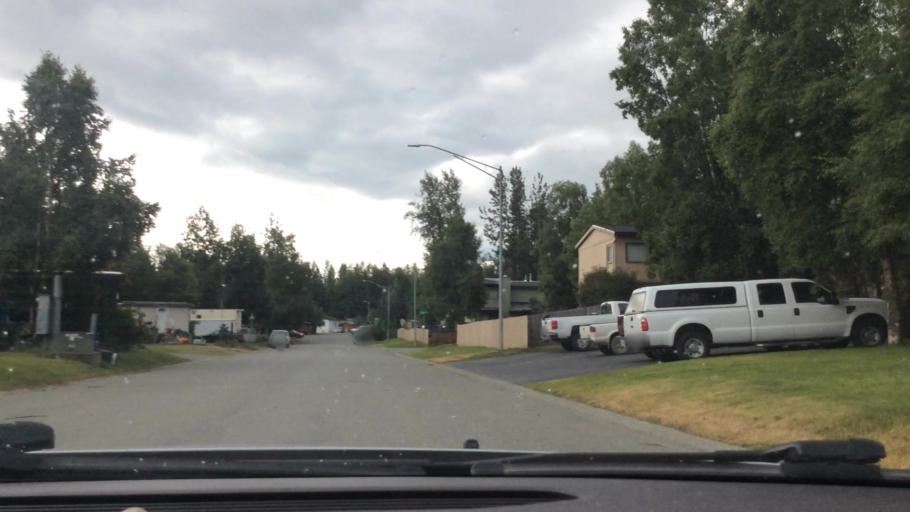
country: US
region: Alaska
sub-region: Anchorage Municipality
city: Anchorage
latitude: 61.1906
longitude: -149.7758
